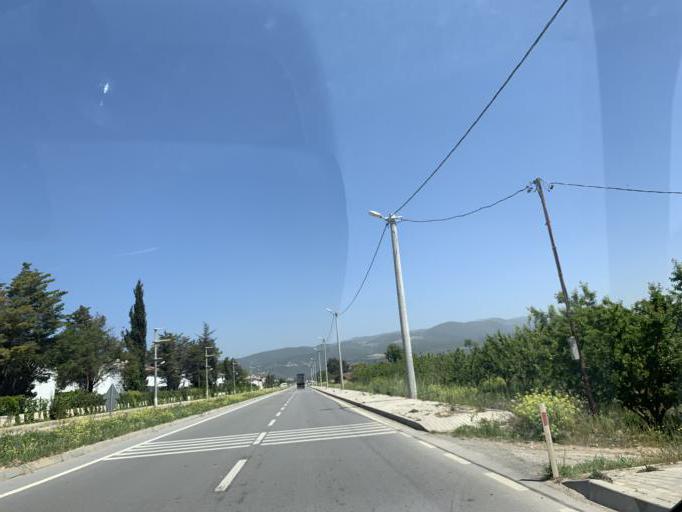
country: TR
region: Bursa
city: Iznik
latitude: 40.4075
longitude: 29.7045
